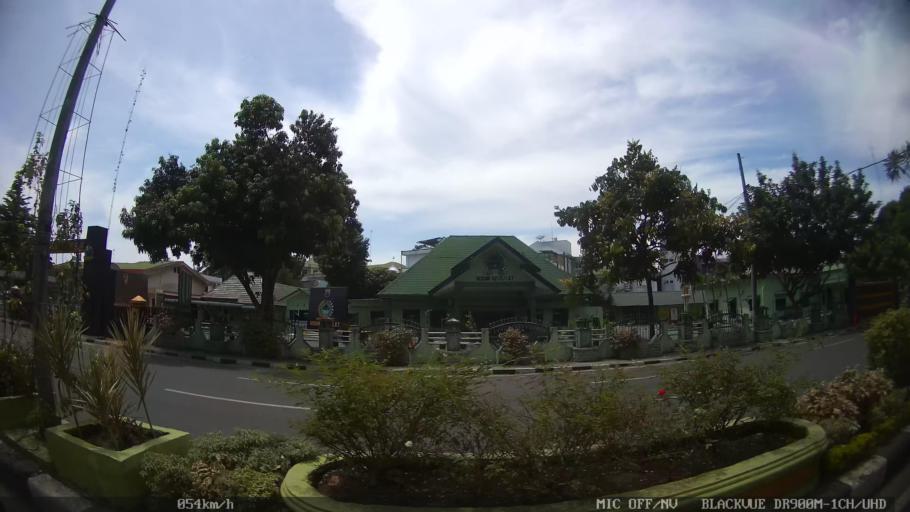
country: ID
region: North Sumatra
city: Binjai
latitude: 3.6028
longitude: 98.4821
